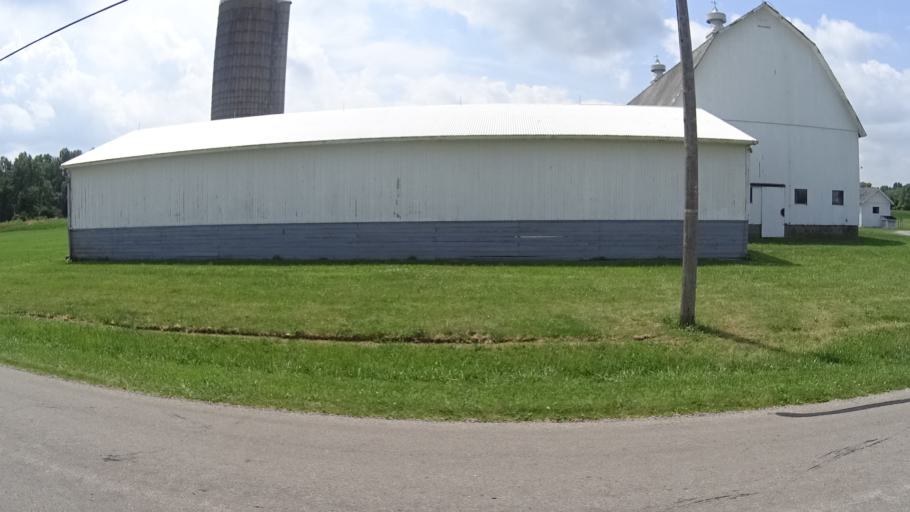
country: US
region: Ohio
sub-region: Lorain County
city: Vermilion
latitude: 41.3865
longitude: -82.4008
